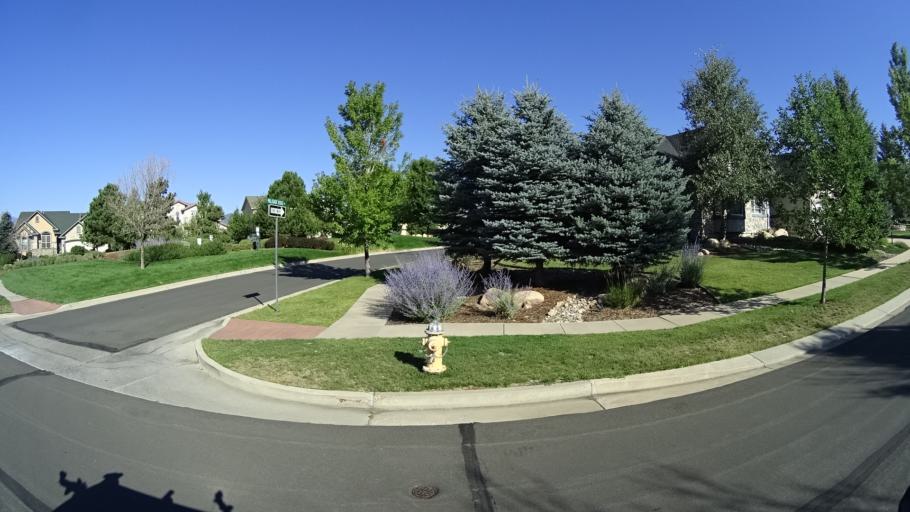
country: US
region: Colorado
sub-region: El Paso County
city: Black Forest
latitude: 38.9774
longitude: -104.7640
